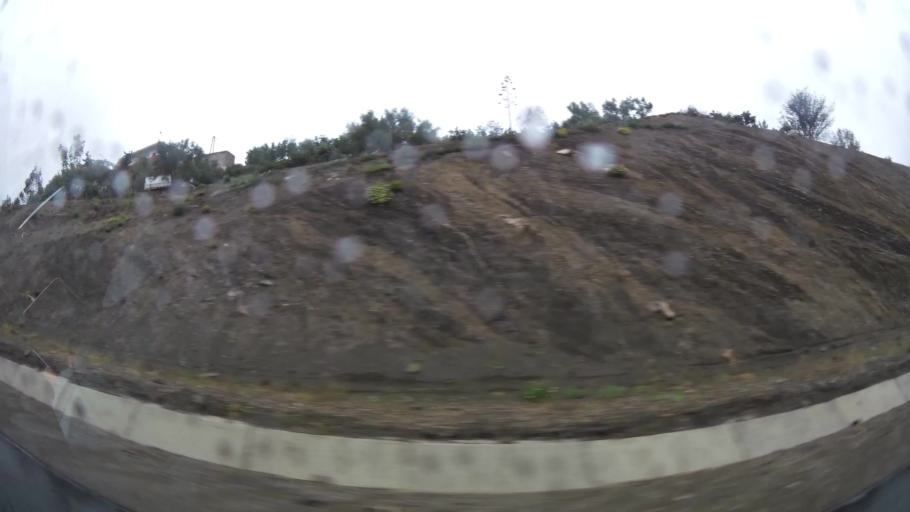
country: MA
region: Taza-Al Hoceima-Taounate
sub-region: Taza
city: Aknoul
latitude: 34.7922
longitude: -3.7520
